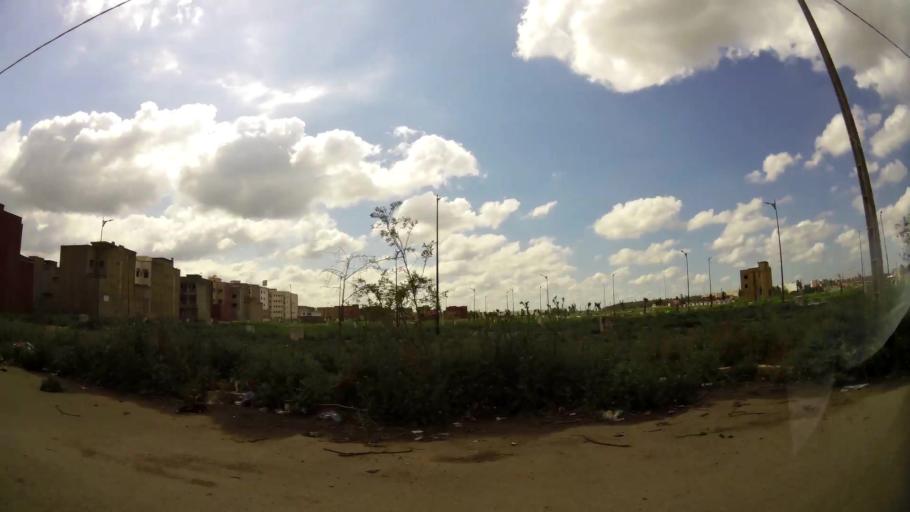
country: MA
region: Grand Casablanca
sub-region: Mediouna
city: Mediouna
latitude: 33.3642
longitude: -7.5336
